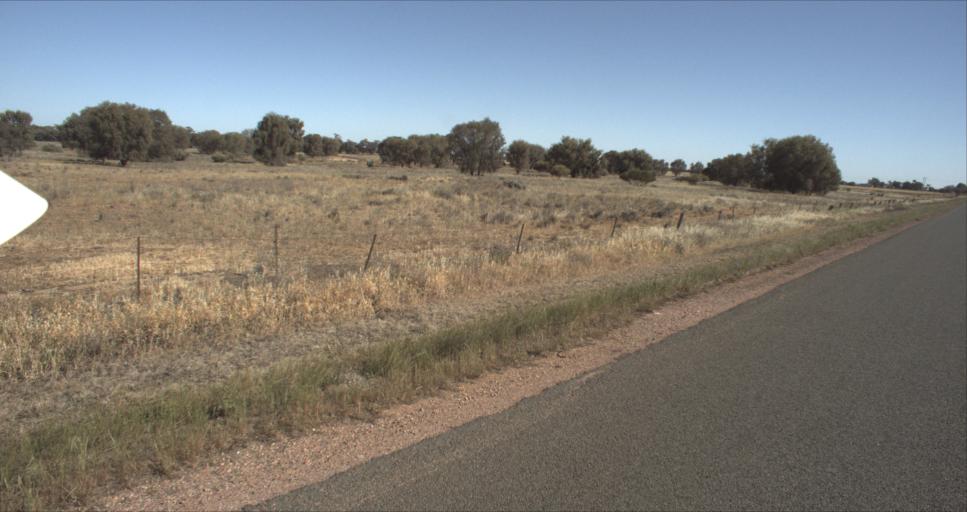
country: AU
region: New South Wales
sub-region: Leeton
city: Leeton
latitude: -34.5663
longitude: 146.2644
